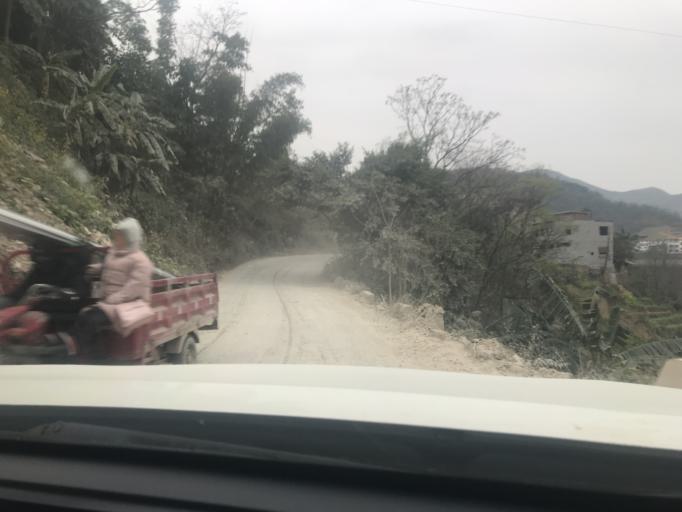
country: CN
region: Guangxi Zhuangzu Zizhiqu
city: Xinzhou
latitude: 24.9858
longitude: 105.8203
